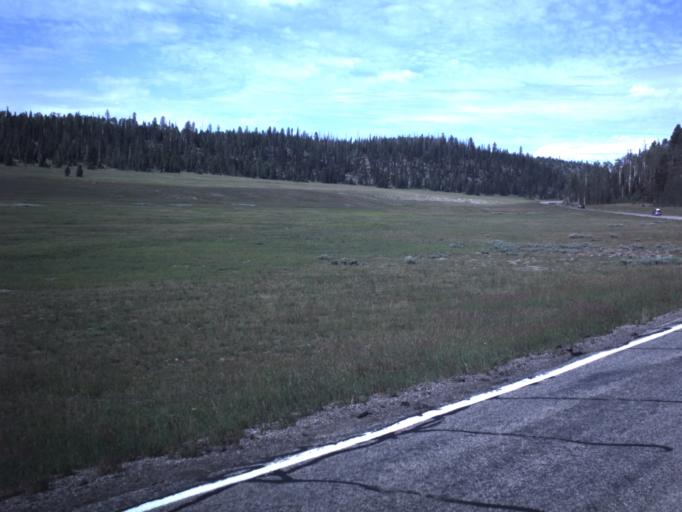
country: US
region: Utah
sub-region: Iron County
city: Parowan
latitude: 37.5712
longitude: -112.8083
